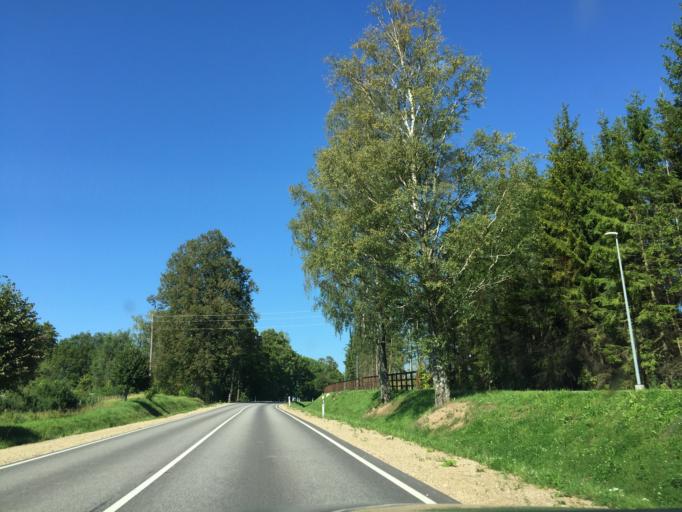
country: LV
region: Limbazu Rajons
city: Limbazi
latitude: 57.4900
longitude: 24.7091
